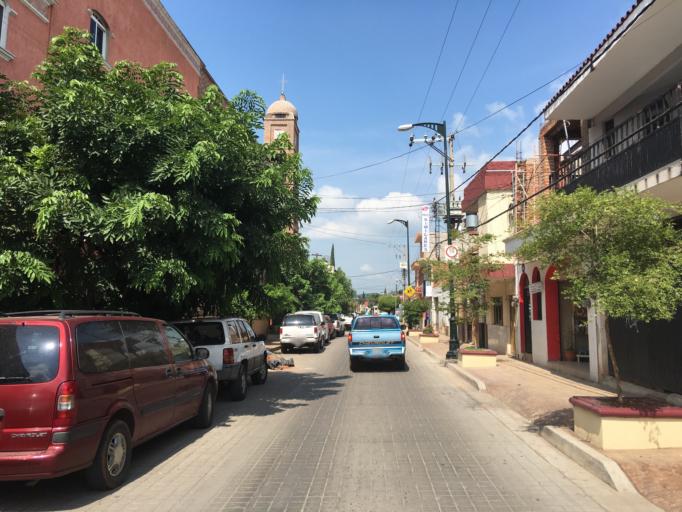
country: MX
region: Jalisco
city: Atotonilco el Alto
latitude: 20.5488
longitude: -102.5124
